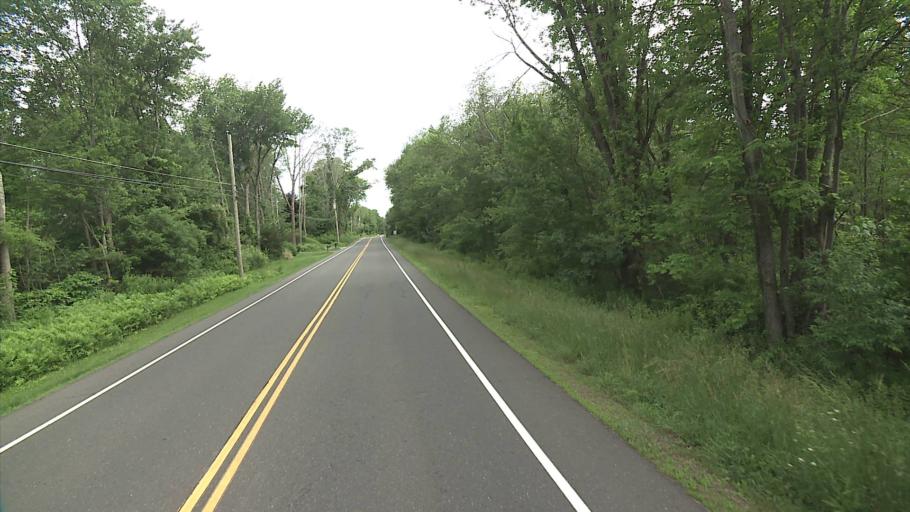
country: US
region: Connecticut
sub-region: Litchfield County
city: Bethlehem Village
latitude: 41.6762
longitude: -73.1746
